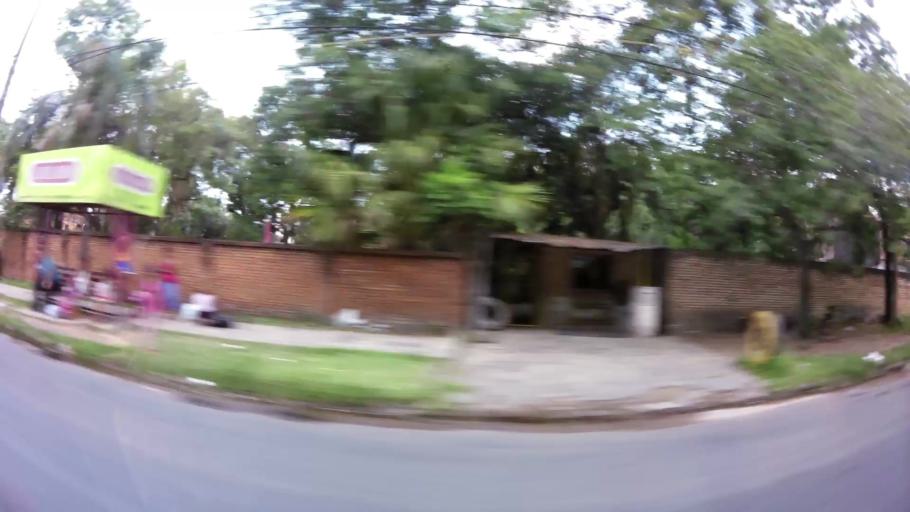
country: PY
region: Central
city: Lambare
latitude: -25.3395
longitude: -57.6352
